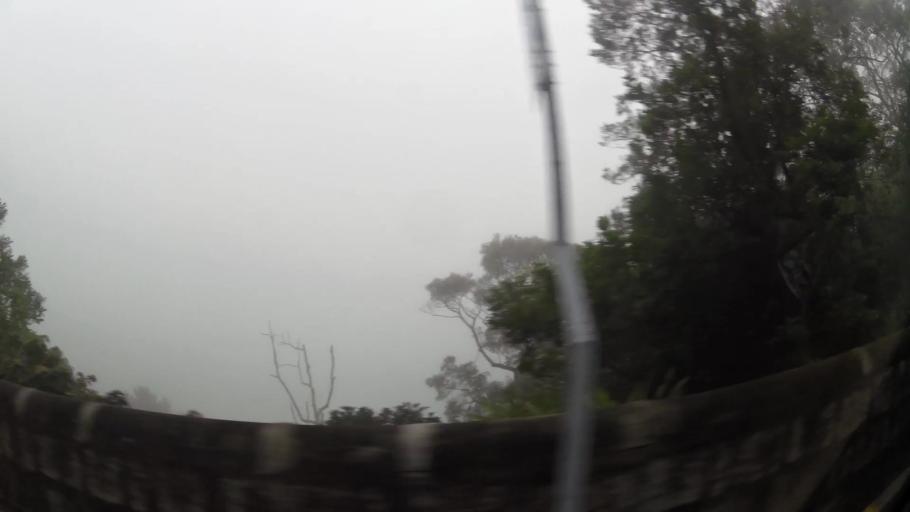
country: HK
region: Central and Western
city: Central
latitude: 22.2696
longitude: 114.1500
